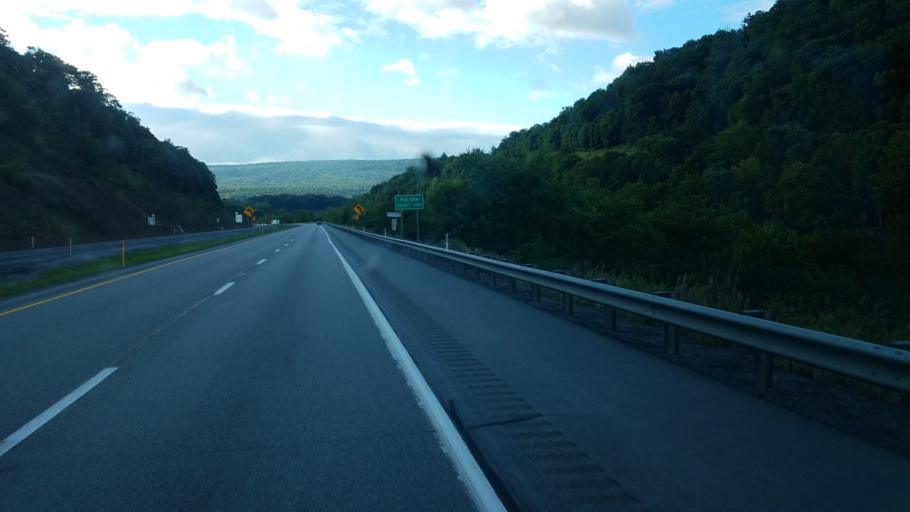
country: US
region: Pennsylvania
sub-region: Bedford County
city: Earlston
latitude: 39.9527
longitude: -78.2393
